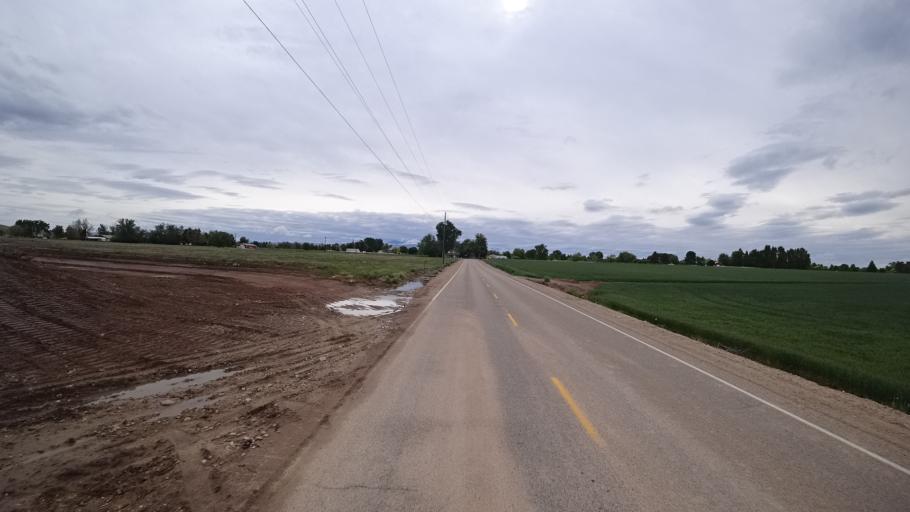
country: US
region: Idaho
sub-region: Ada County
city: Star
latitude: 43.7175
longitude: -116.4862
